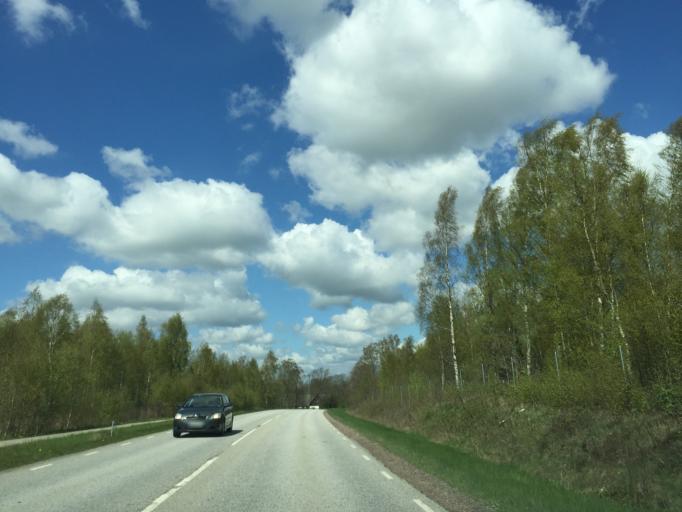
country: SE
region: Skane
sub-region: Lunds Kommun
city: Genarp
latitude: 55.7001
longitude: 13.3460
